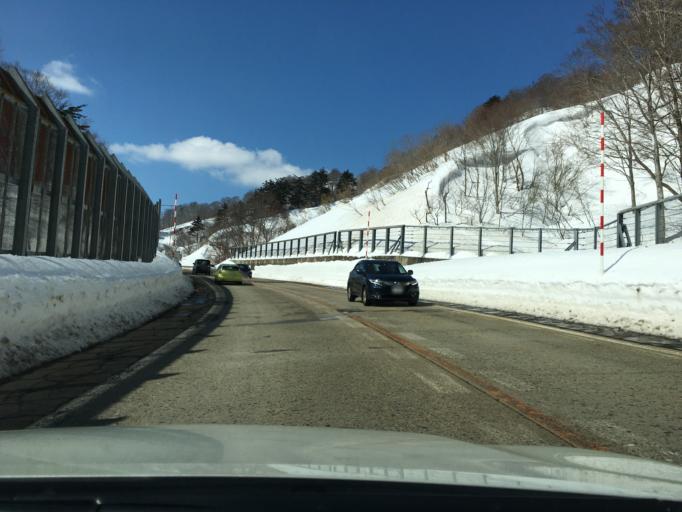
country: JP
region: Yamagata
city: Tsuruoka
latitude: 38.4912
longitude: 139.9840
